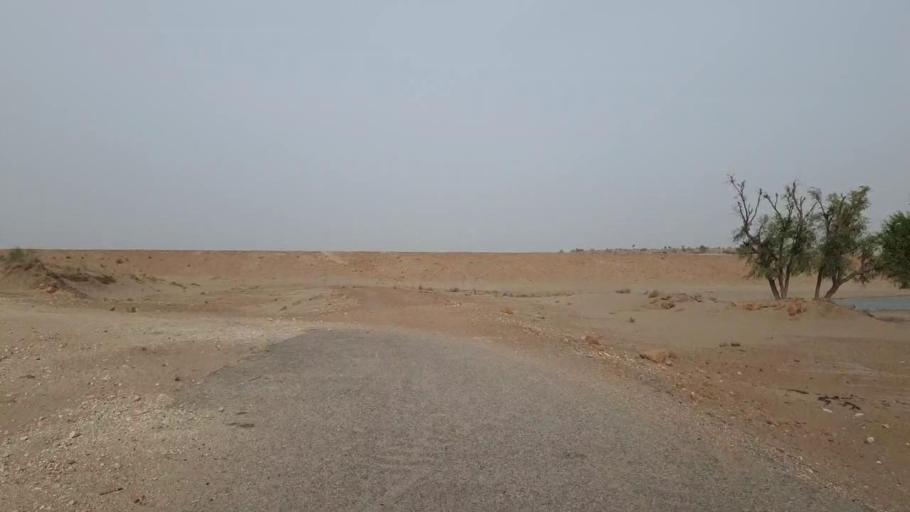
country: PK
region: Sindh
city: Islamkot
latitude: 24.5435
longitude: 70.3810
